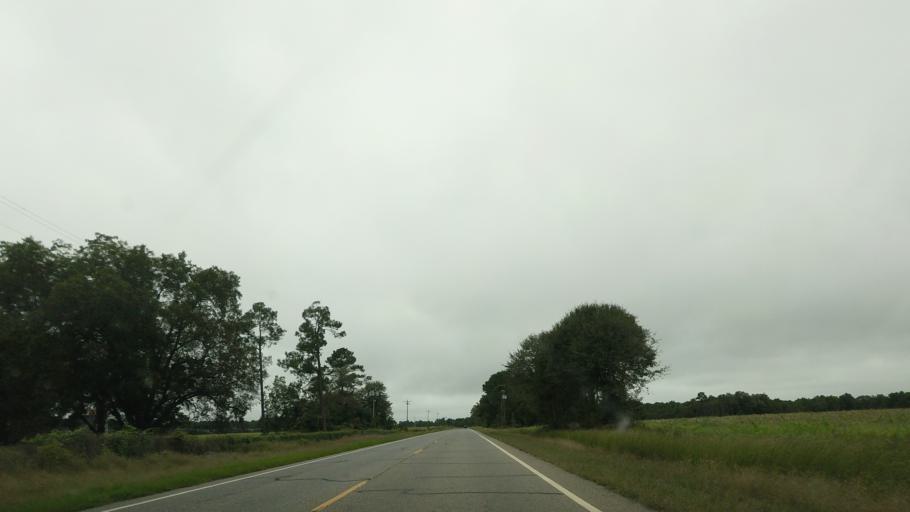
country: US
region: Georgia
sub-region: Irwin County
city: Ocilla
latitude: 31.5263
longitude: -83.2456
